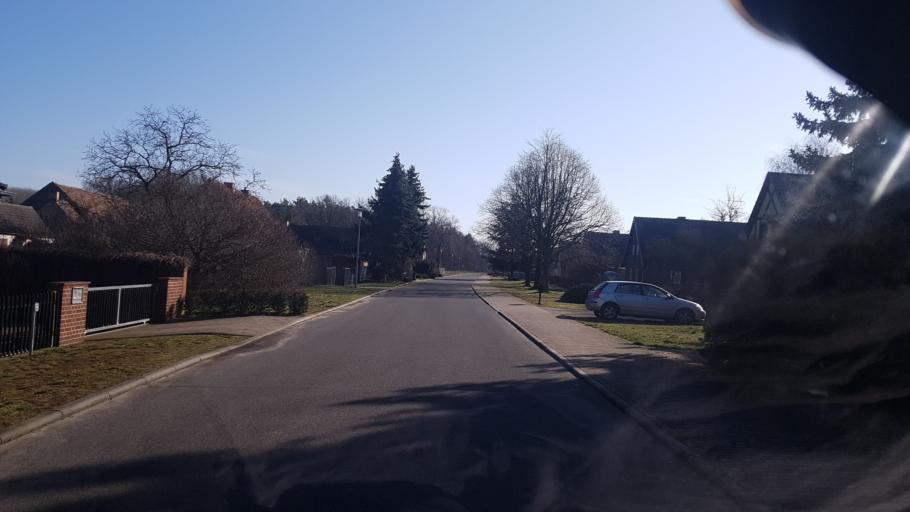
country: DE
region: Brandenburg
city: Luckau
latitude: 51.8344
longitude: 13.8021
